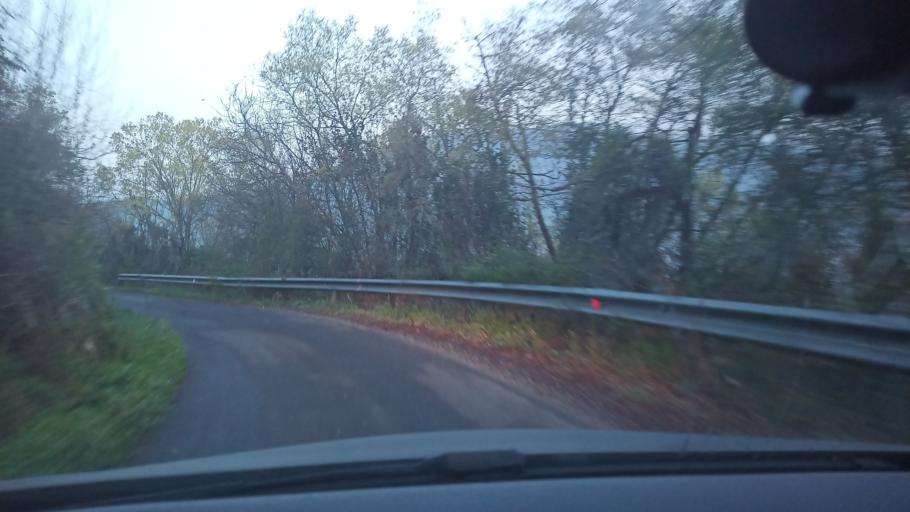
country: IT
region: Latium
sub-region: Provincia di Rieti
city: Cottanello
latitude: 42.4075
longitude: 12.6822
